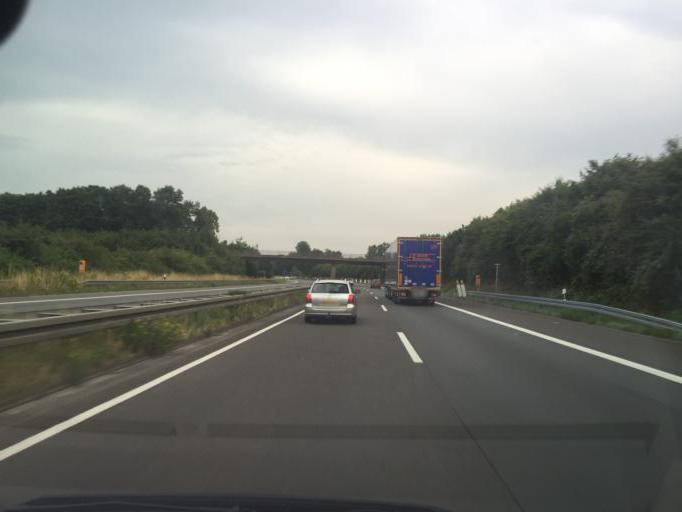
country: DE
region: North Rhine-Westphalia
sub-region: Regierungsbezirk Dusseldorf
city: Nettetal
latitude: 51.2901
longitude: 6.2658
